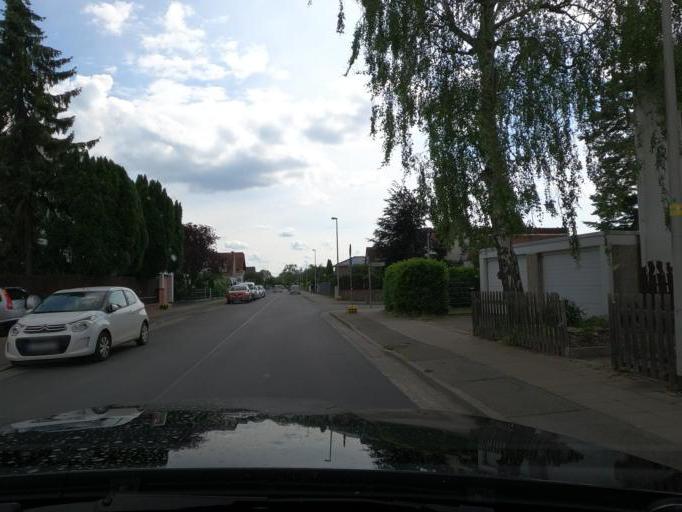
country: DE
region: Lower Saxony
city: Isernhagen Farster Bauerschaft
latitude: 52.3961
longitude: 9.8367
